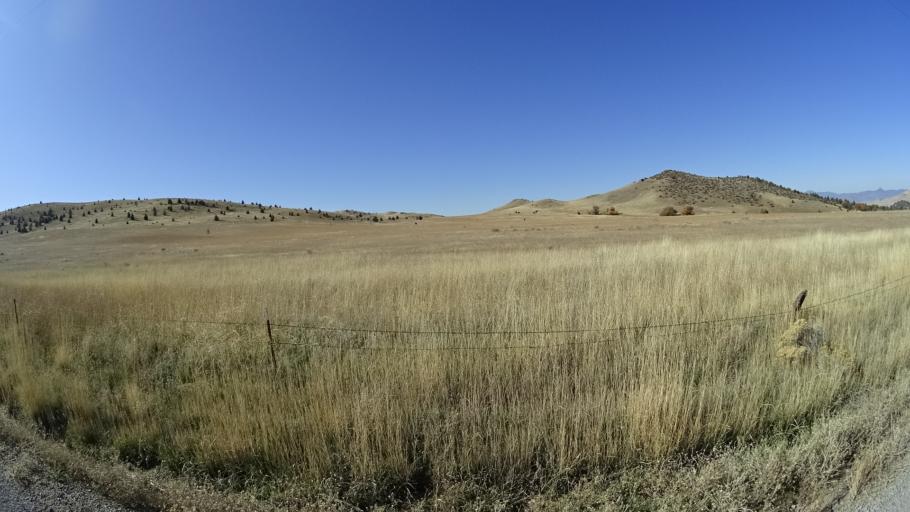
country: US
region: California
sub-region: Siskiyou County
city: Montague
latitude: 41.7825
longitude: -122.3591
